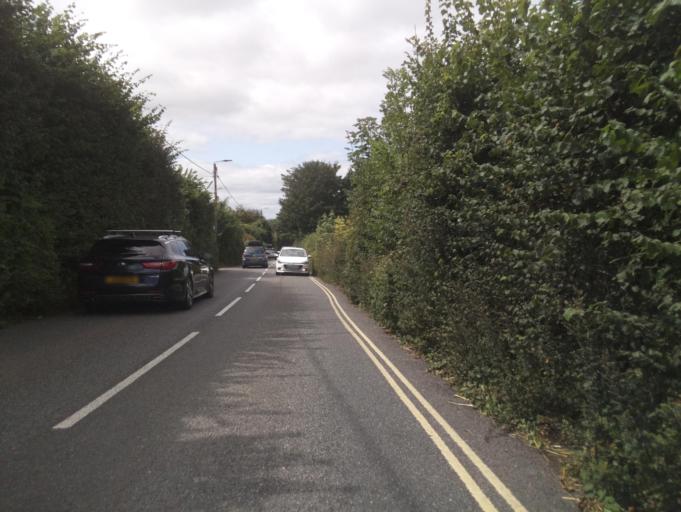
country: GB
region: England
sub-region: Devon
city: Teignmouth
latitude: 50.5386
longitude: -3.5055
